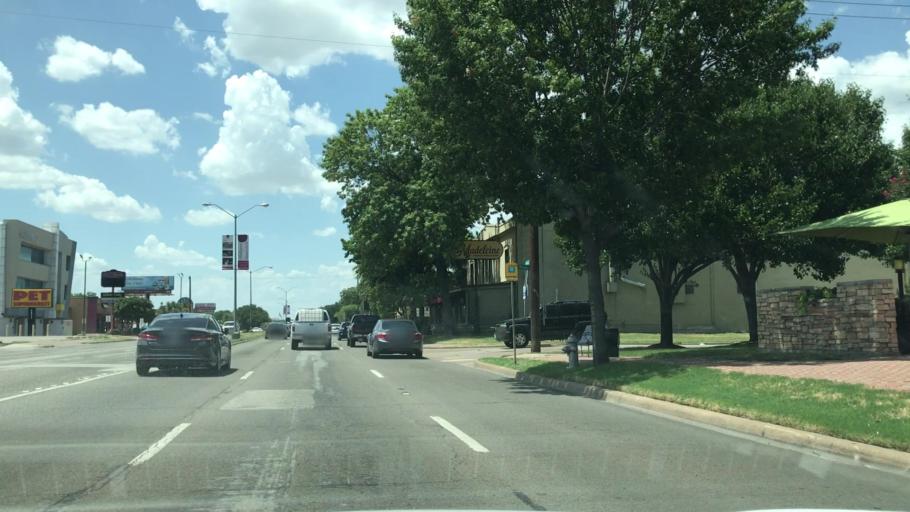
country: US
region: Texas
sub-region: Dallas County
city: Highland Park
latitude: 32.8127
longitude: -96.8064
